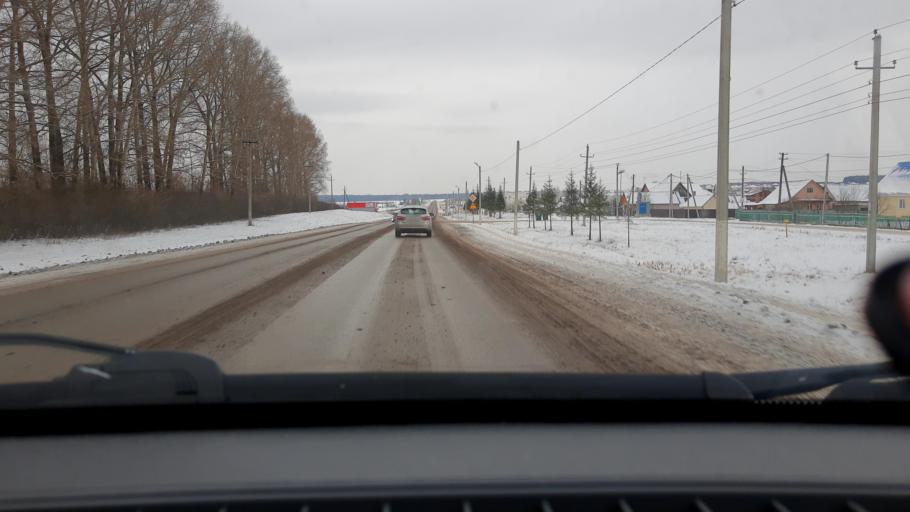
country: RU
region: Bashkortostan
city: Iglino
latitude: 54.8074
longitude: 56.4096
